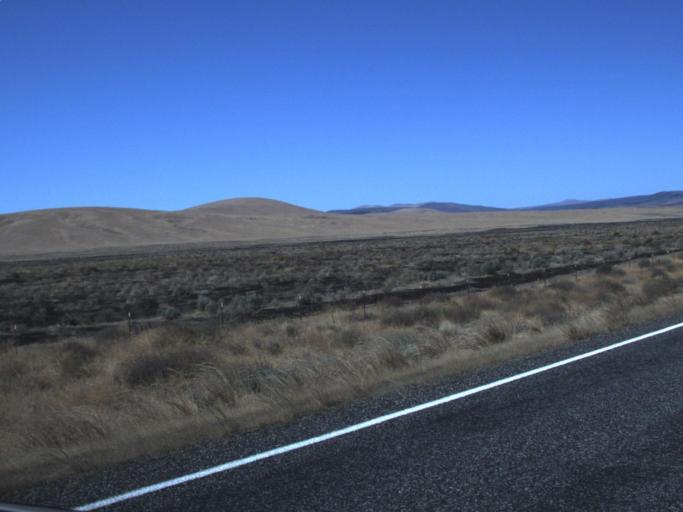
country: US
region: Washington
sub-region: Grant County
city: Desert Aire
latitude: 46.5206
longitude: -119.6725
